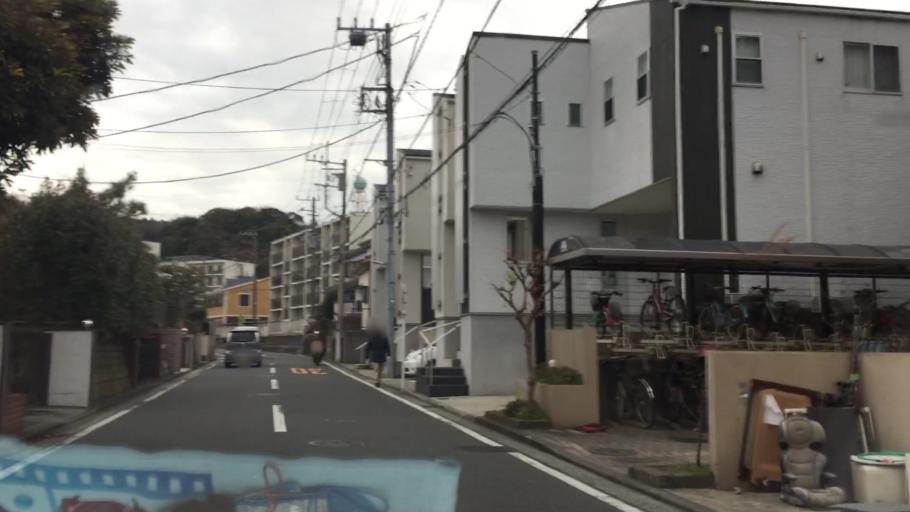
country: JP
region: Kanagawa
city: Yokosuka
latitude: 35.3420
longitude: 139.6332
